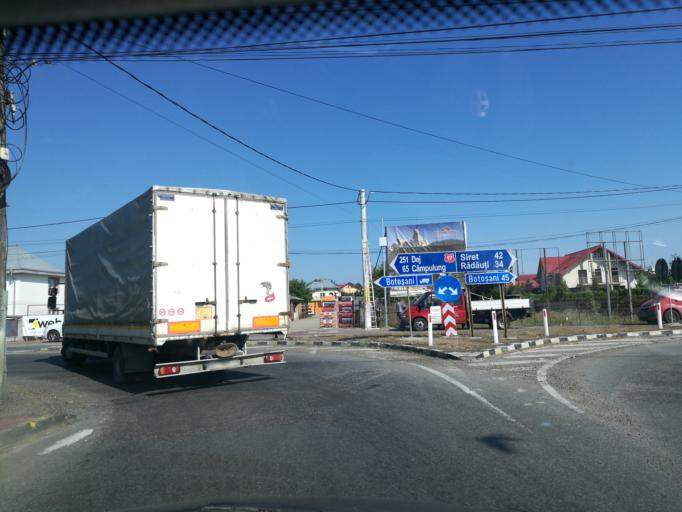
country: RO
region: Suceava
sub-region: Comuna Scheia
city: Scheia
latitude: 47.6529
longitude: 26.2256
